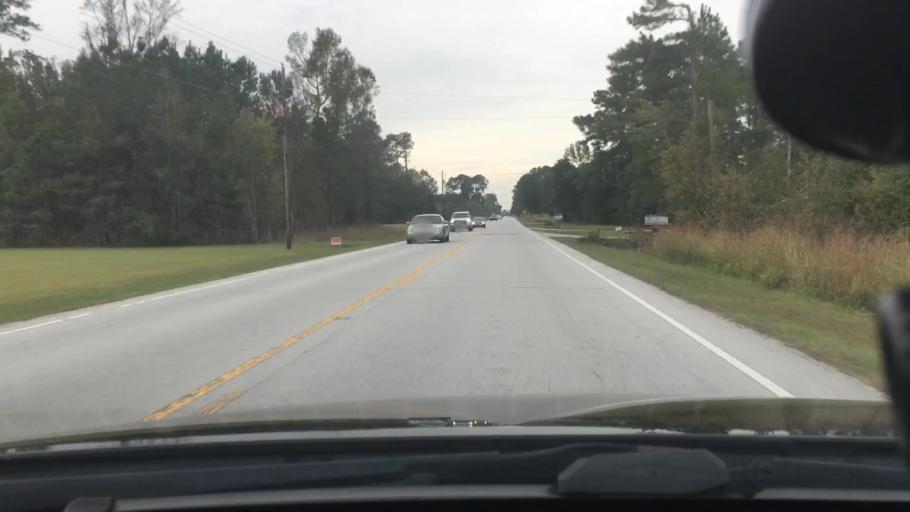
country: US
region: North Carolina
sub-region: Craven County
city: Vanceboro
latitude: 35.3550
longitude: -77.1918
